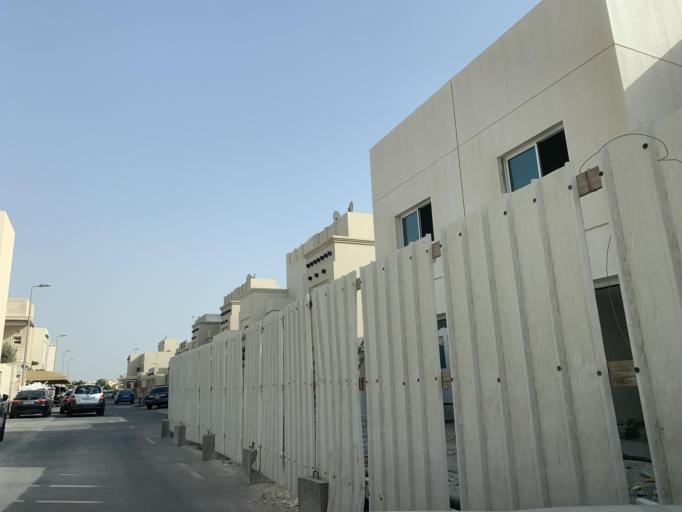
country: BH
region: Manama
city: Jidd Hafs
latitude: 26.2283
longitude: 50.4441
